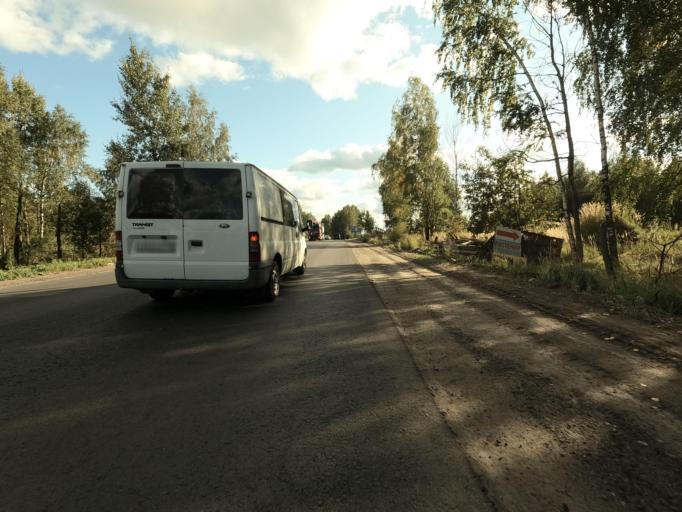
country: RU
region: Leningrad
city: Koltushi
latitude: 59.9258
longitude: 30.6639
